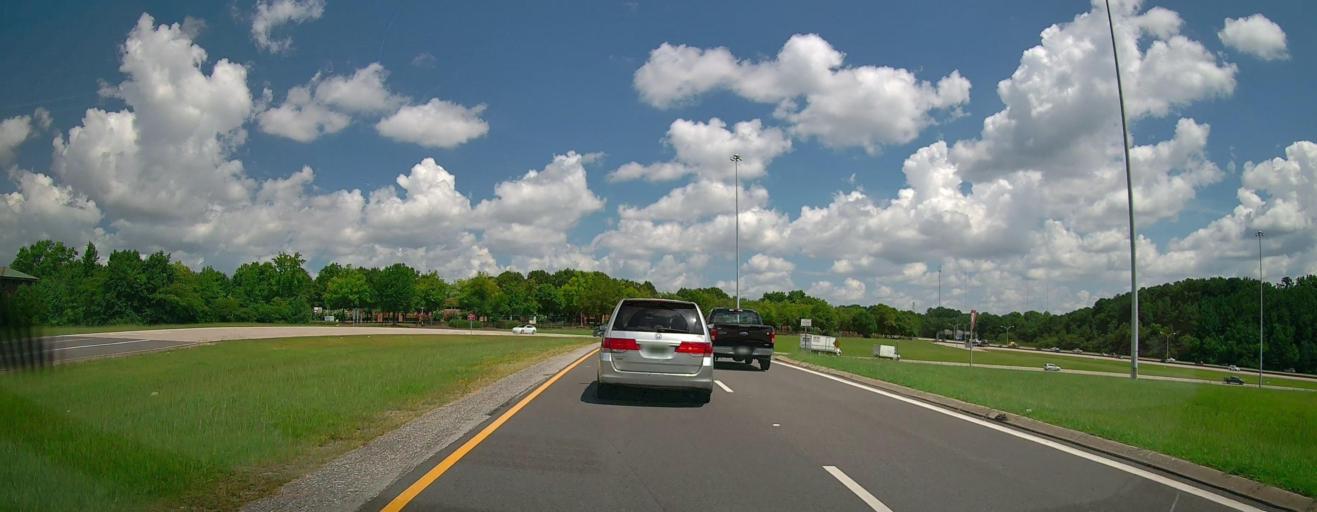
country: US
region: Alabama
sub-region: Jefferson County
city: Homewood
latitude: 33.4508
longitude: -86.8191
